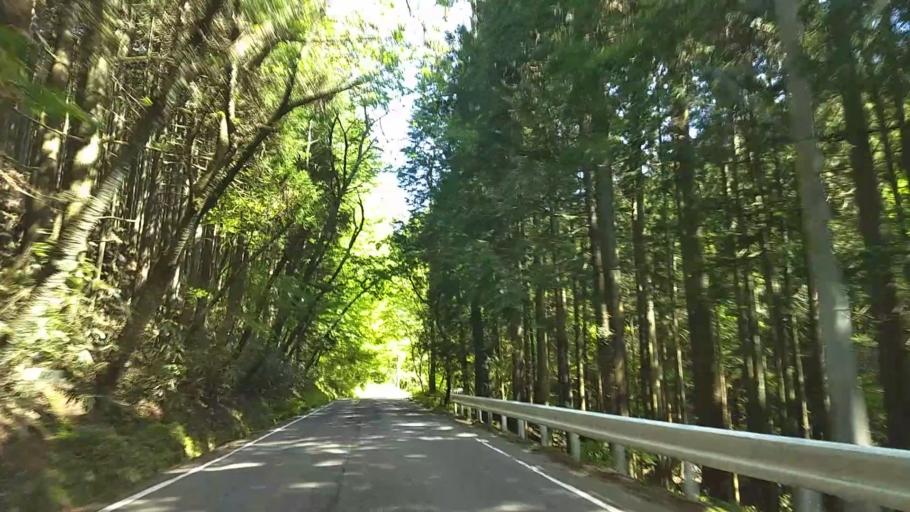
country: JP
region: Shizuoka
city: Gotemba
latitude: 35.2858
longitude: 138.9694
